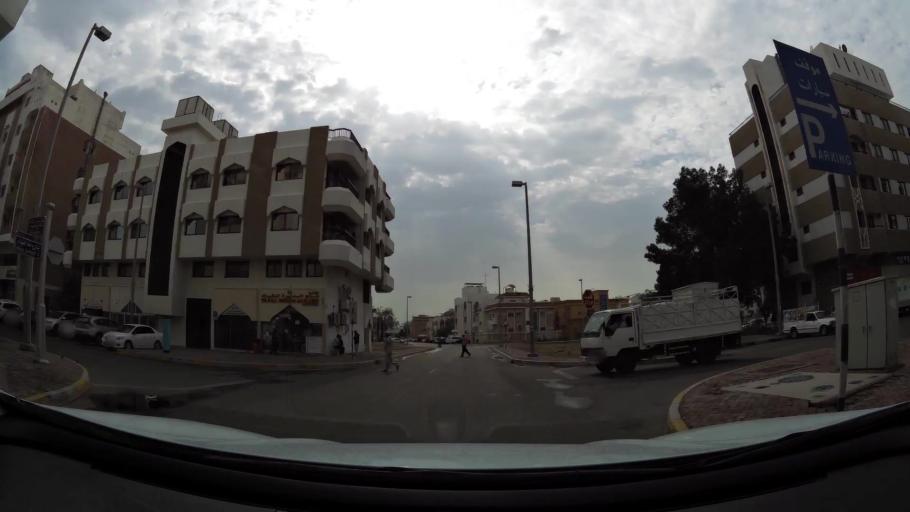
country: AE
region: Abu Dhabi
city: Abu Dhabi
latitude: 24.4449
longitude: 54.4048
